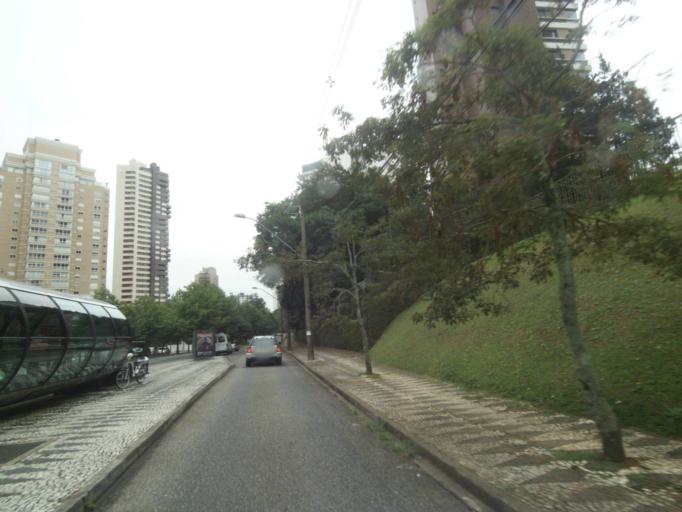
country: BR
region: Parana
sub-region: Curitiba
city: Curitiba
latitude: -25.4375
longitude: -49.3242
